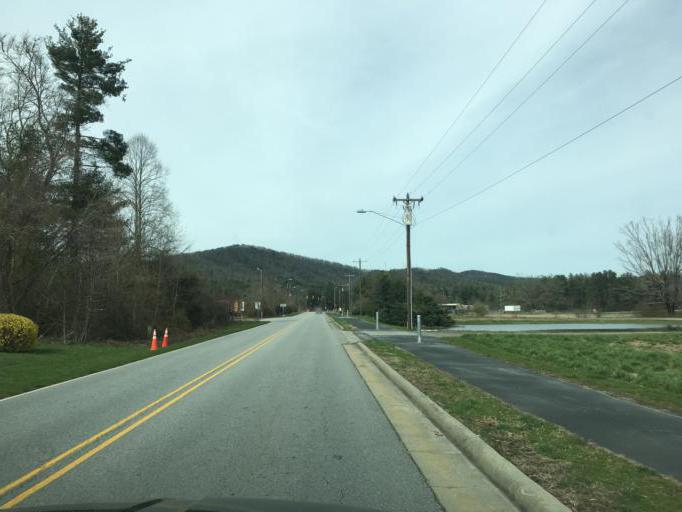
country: US
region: North Carolina
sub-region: Transylvania County
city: Brevard
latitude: 35.2647
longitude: -82.7061
